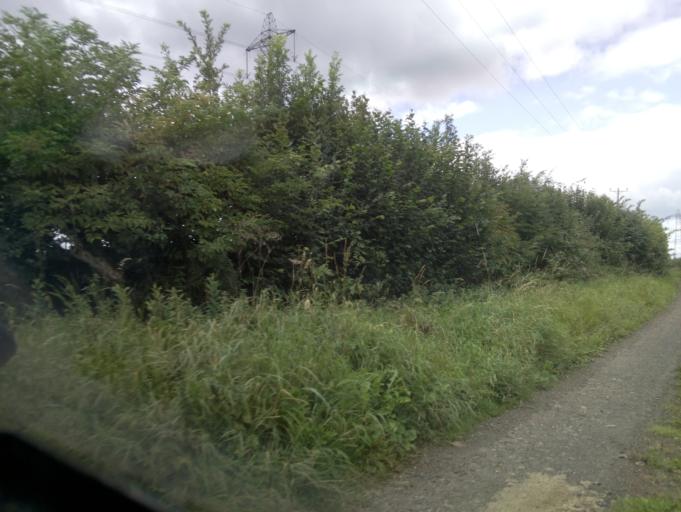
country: GB
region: England
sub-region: Wiltshire
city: Nettleton
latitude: 51.5102
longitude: -2.2294
